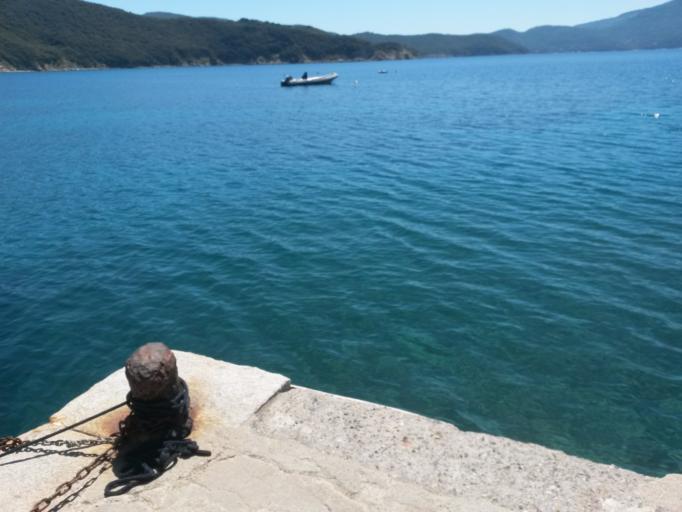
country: IT
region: Tuscany
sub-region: Provincia di Livorno
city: Portoferraio
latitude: 42.8242
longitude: 10.2696
